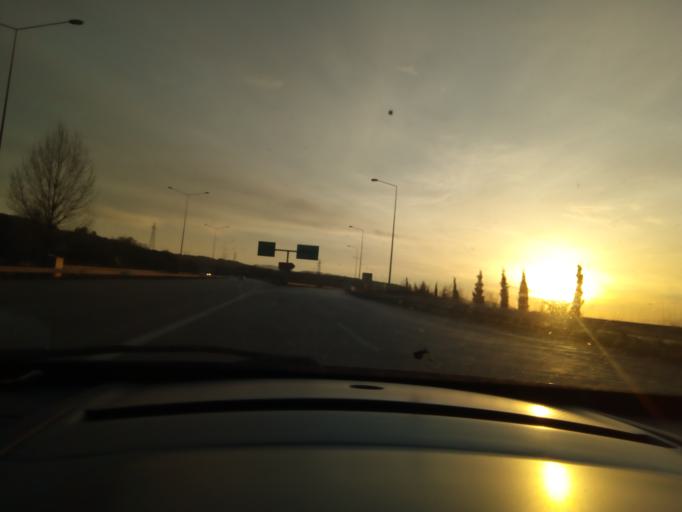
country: TR
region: Bursa
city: Niluefer
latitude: 40.2894
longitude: 29.0202
